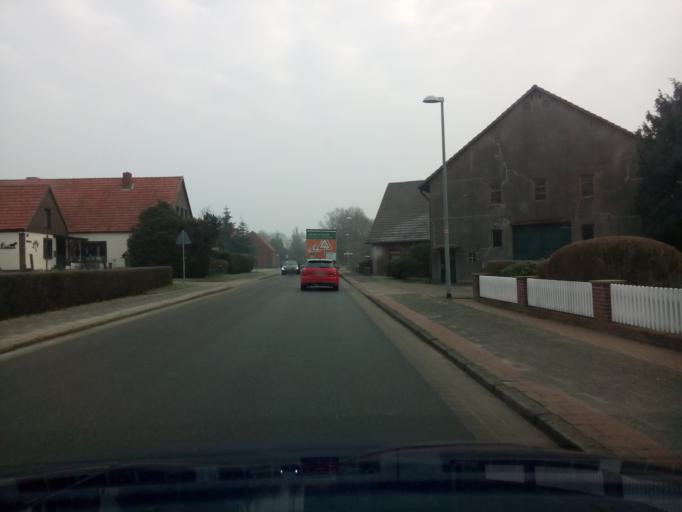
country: DE
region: Lower Saxony
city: Elmlohe
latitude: 53.6088
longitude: 8.6848
